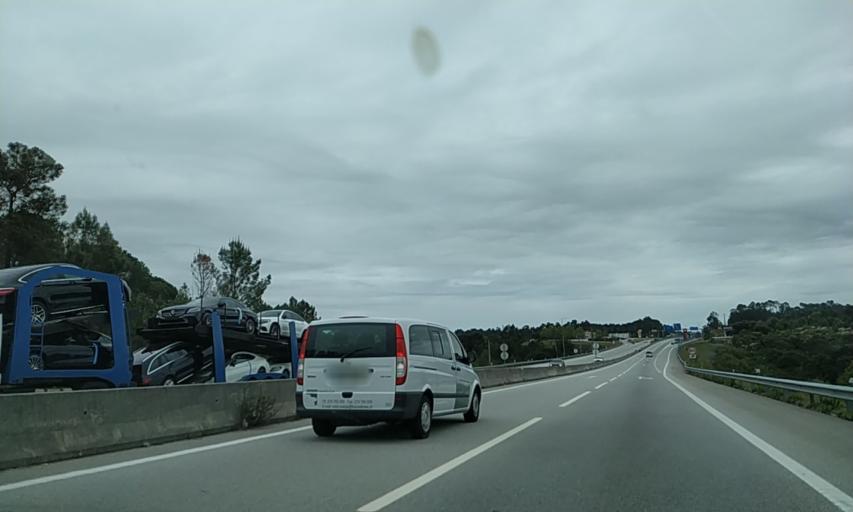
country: PT
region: Viseu
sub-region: Viseu
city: Viseu
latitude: 40.6241
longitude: -7.9390
